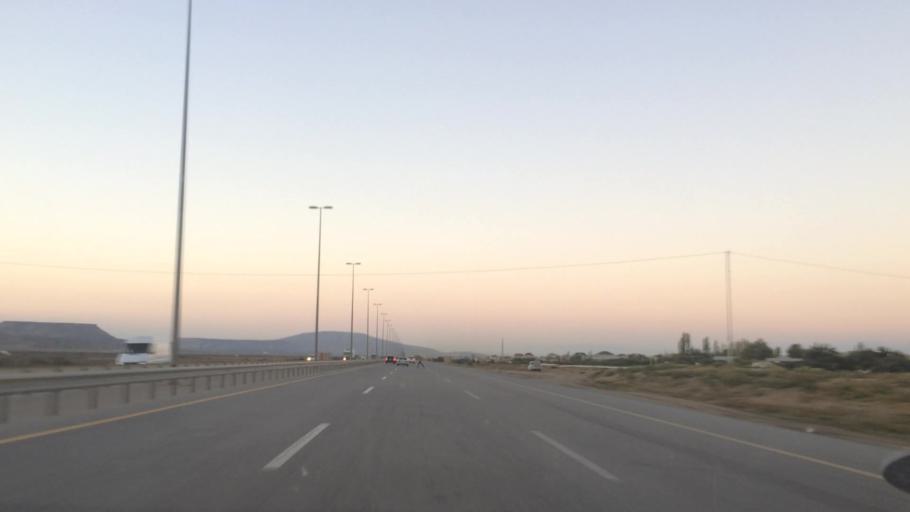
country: AZ
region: Baki
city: Qobustan
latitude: 40.0214
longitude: 49.4249
